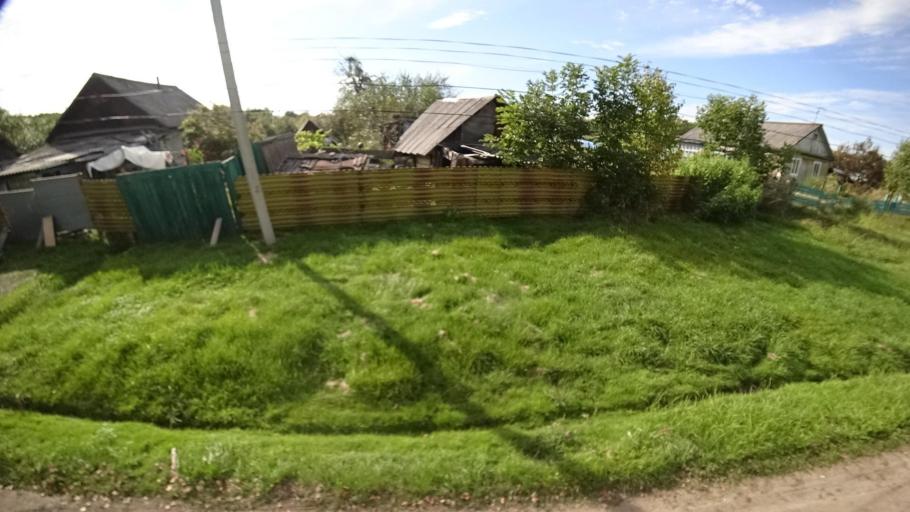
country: RU
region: Primorskiy
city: Dostoyevka
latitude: 44.2958
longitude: 133.4594
